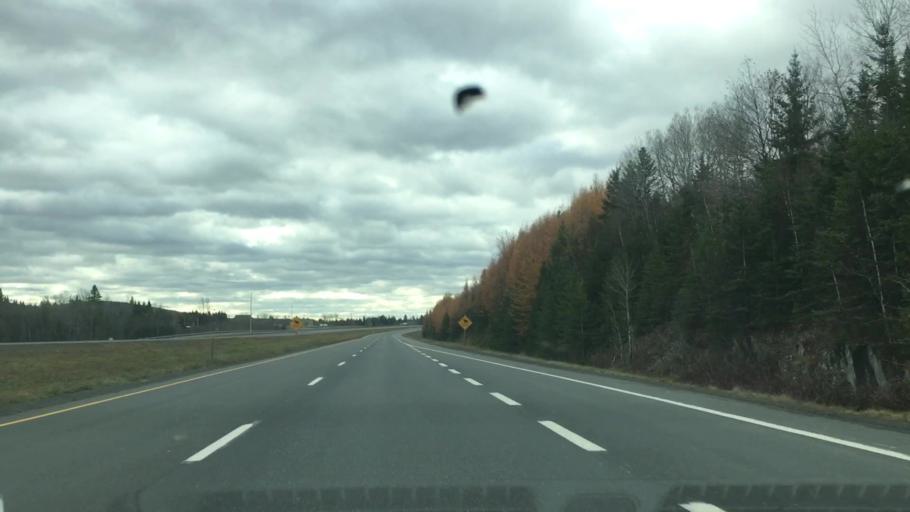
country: US
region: Maine
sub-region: Aroostook County
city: Fort Fairfield
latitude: 46.7464
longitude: -67.7149
